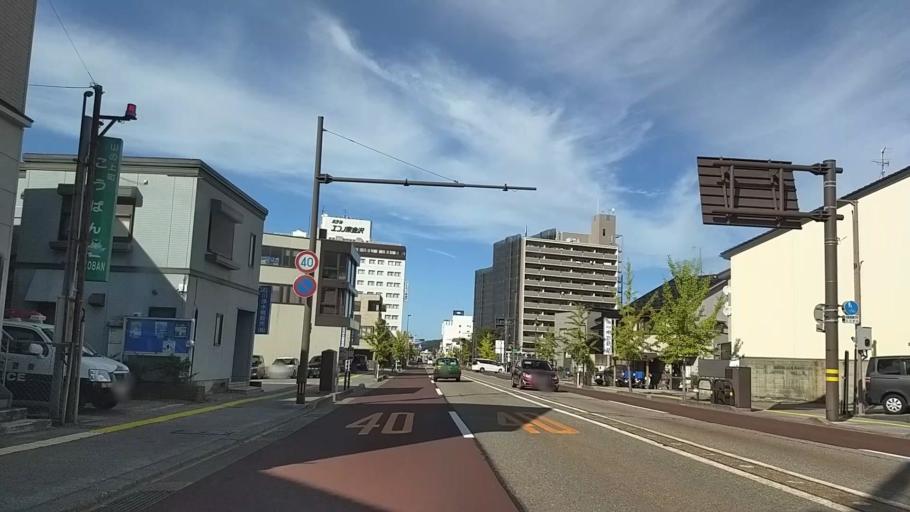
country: JP
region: Ishikawa
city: Kanazawa-shi
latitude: 36.5802
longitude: 136.6705
